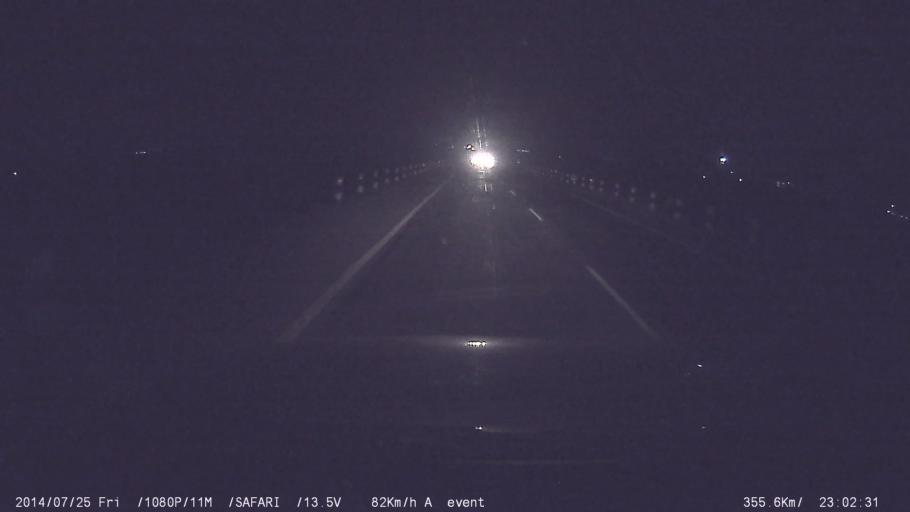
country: IN
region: Tamil Nadu
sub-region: Coimbatore
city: Chettipalaiyam
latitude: 10.9373
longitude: 77.0050
